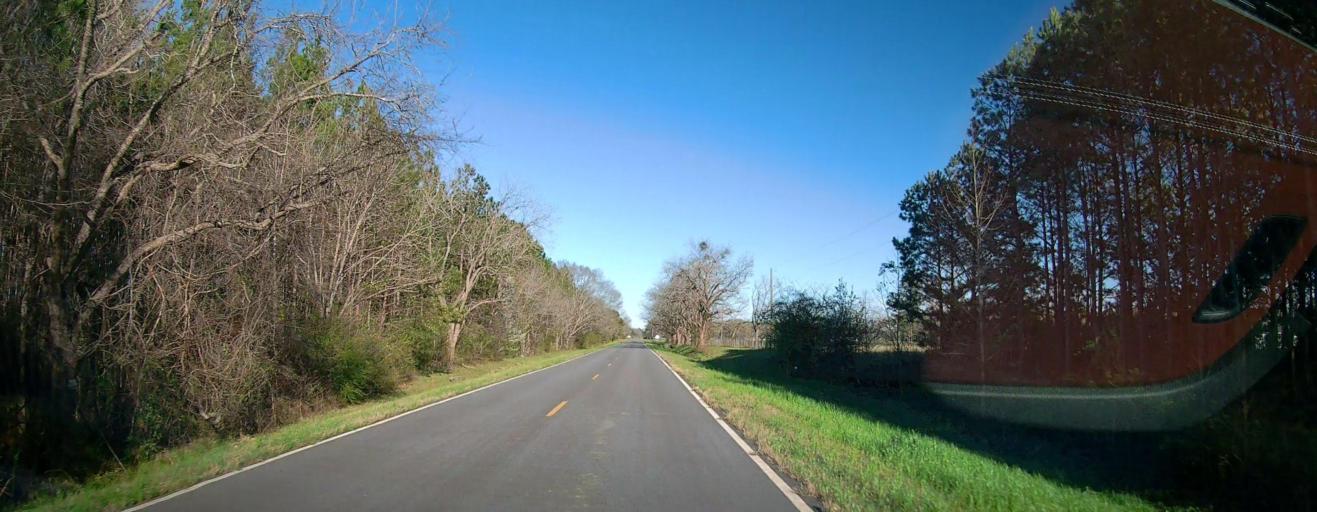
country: US
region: Georgia
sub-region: Pulaski County
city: Hawkinsville
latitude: 32.3479
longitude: -83.6044
